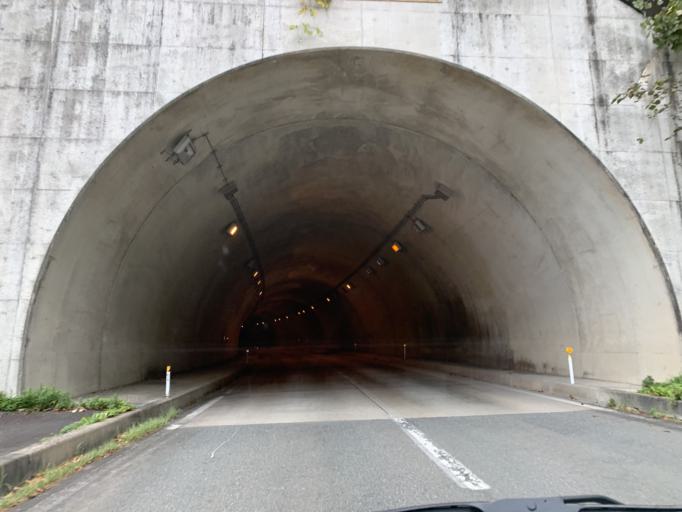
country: JP
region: Iwate
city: Mizusawa
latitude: 39.1258
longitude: 140.9335
